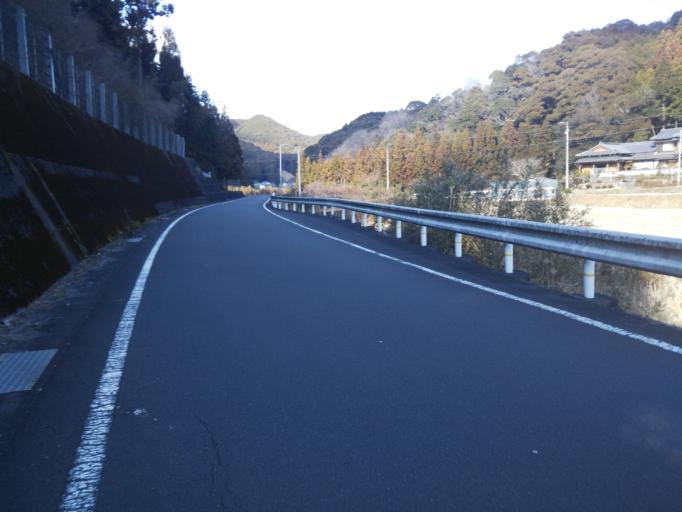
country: JP
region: Kochi
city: Nakamura
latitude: 33.0432
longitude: 132.9708
